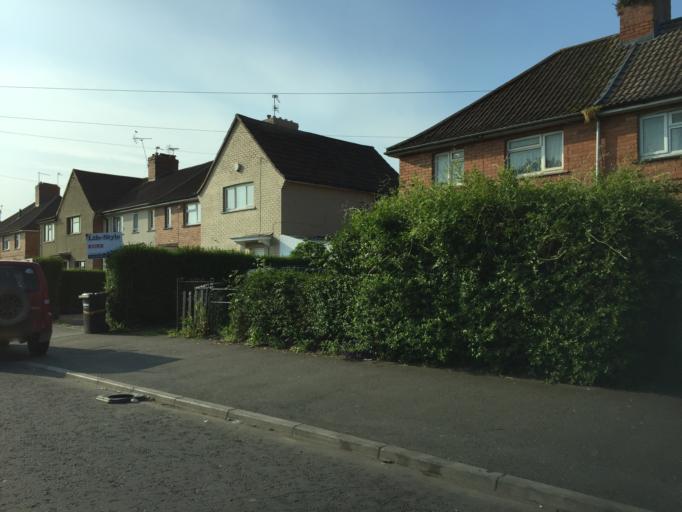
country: GB
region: England
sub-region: Bristol
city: Bristol
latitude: 51.4999
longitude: -2.6054
